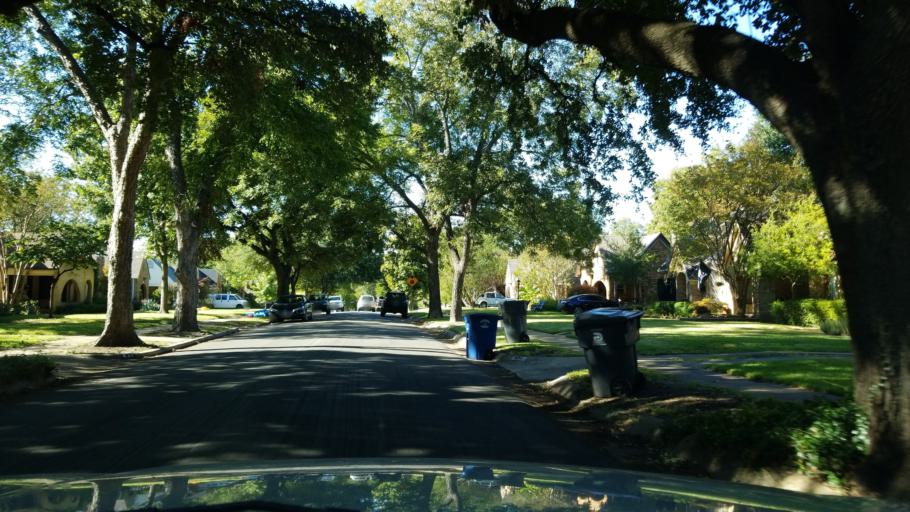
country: US
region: Texas
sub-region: Dallas County
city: Highland Park
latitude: 32.8065
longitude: -96.7436
